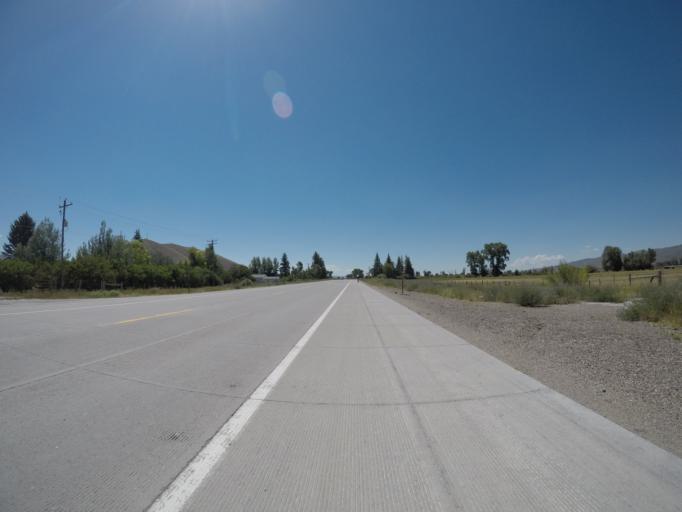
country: US
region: Idaho
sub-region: Bear Lake County
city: Montpelier
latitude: 42.0981
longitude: -110.9524
